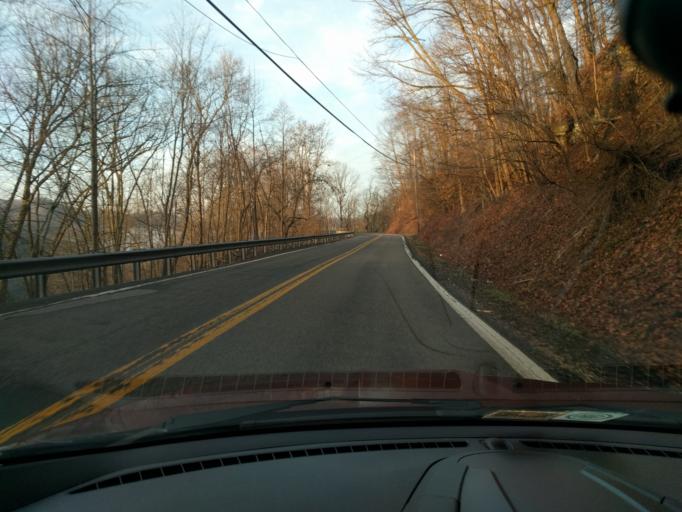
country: US
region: West Virginia
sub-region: Fayette County
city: Ansted
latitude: 38.1422
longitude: -81.1578
